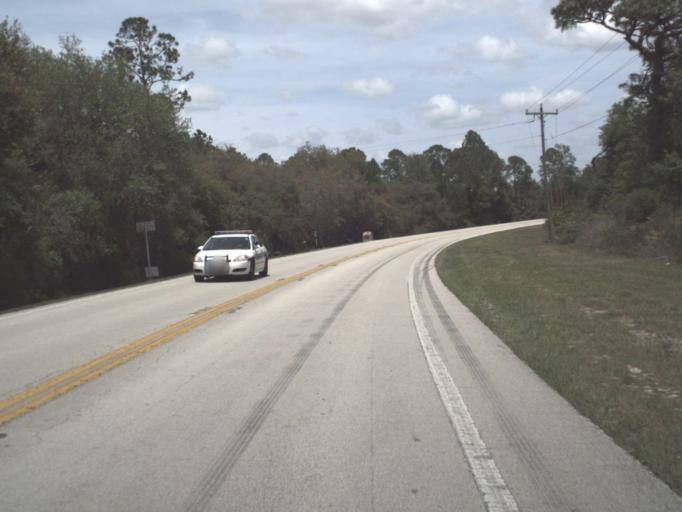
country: US
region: Florida
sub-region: Lake County
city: Lake Mack-Forest Hills
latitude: 28.9044
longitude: -81.4554
